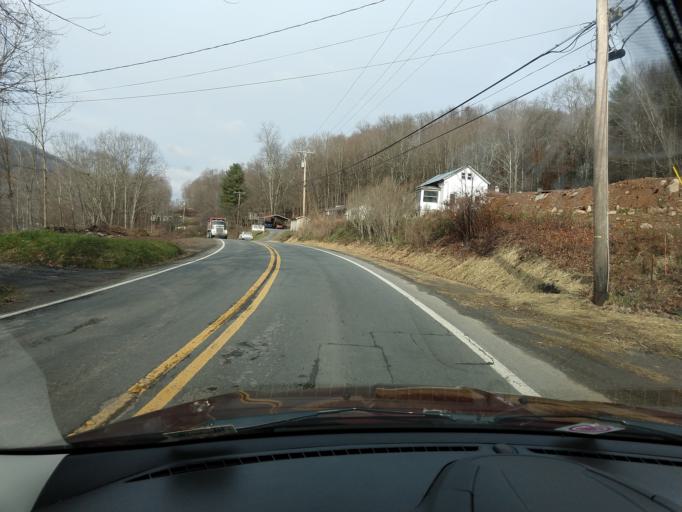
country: US
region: West Virginia
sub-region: Greenbrier County
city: Rainelle
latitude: 37.9681
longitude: -80.7008
